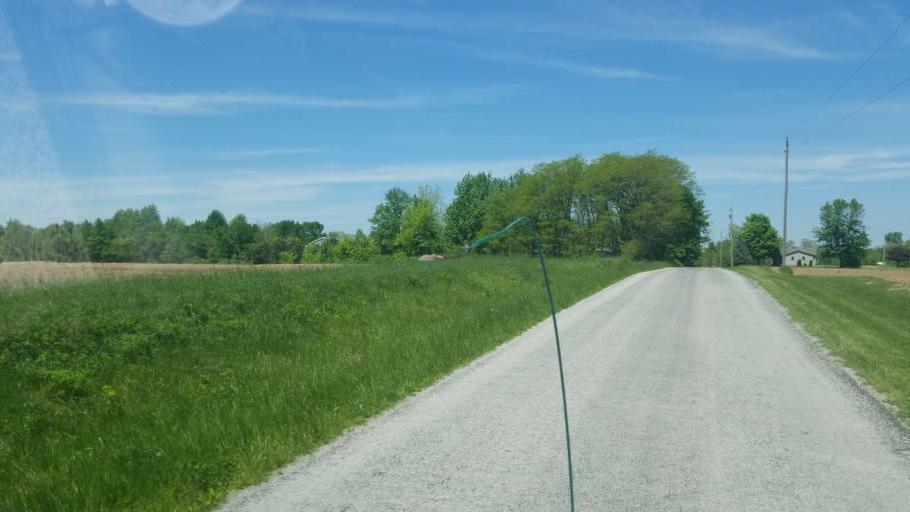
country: US
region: Ohio
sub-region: Huron County
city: Greenwich
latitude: 40.9943
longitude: -82.4329
